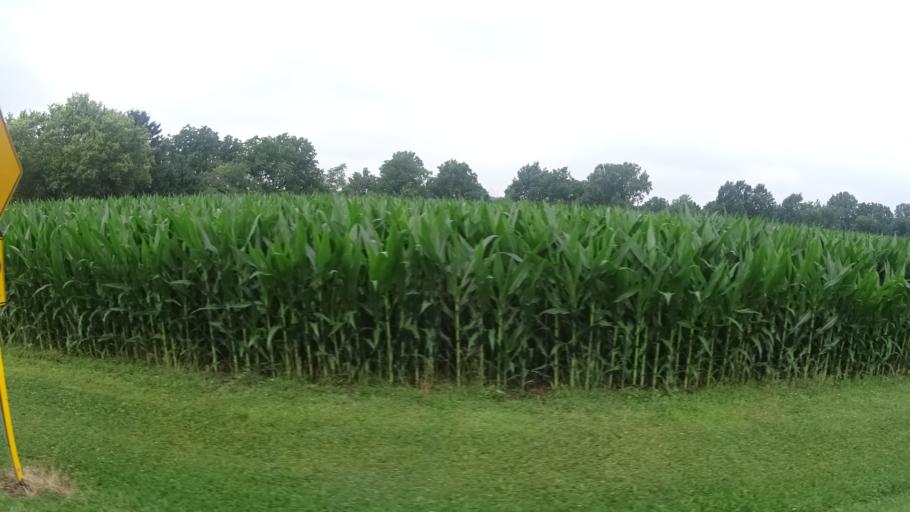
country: US
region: Ohio
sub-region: Erie County
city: Milan
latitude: 41.2888
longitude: -82.5118
